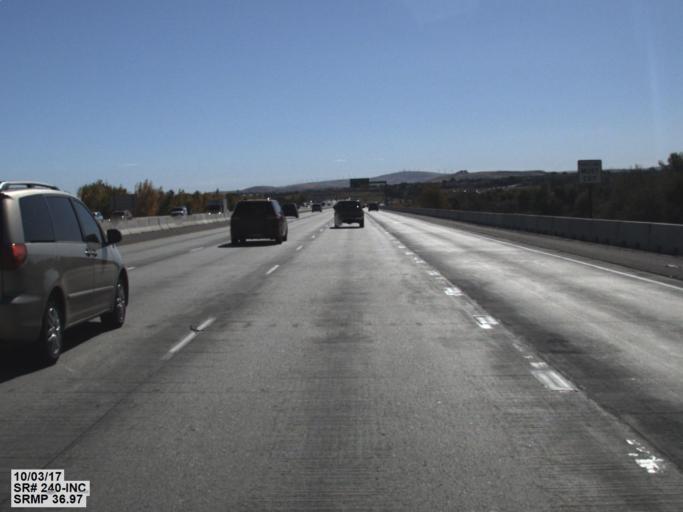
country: US
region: Washington
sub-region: Benton County
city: Richland
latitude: 46.2482
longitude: -119.2529
